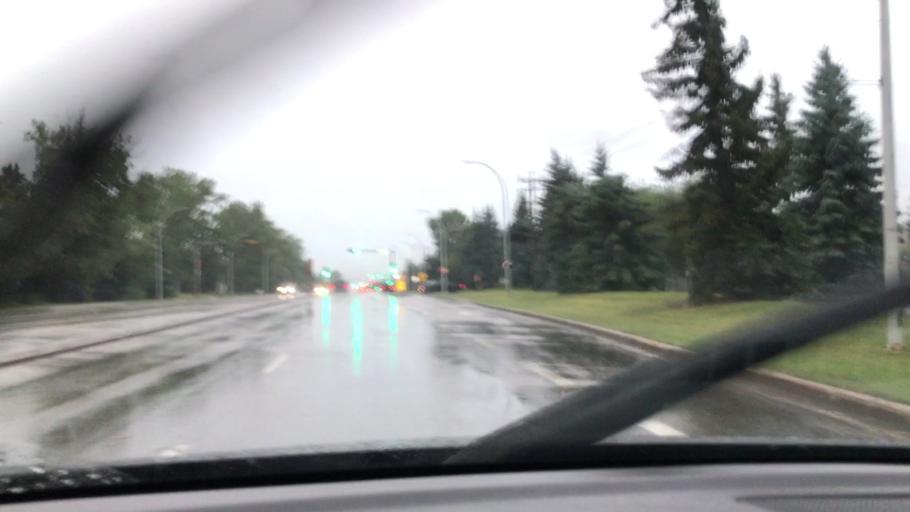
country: CA
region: Alberta
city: Sherwood Park
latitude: 53.5166
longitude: -113.3203
